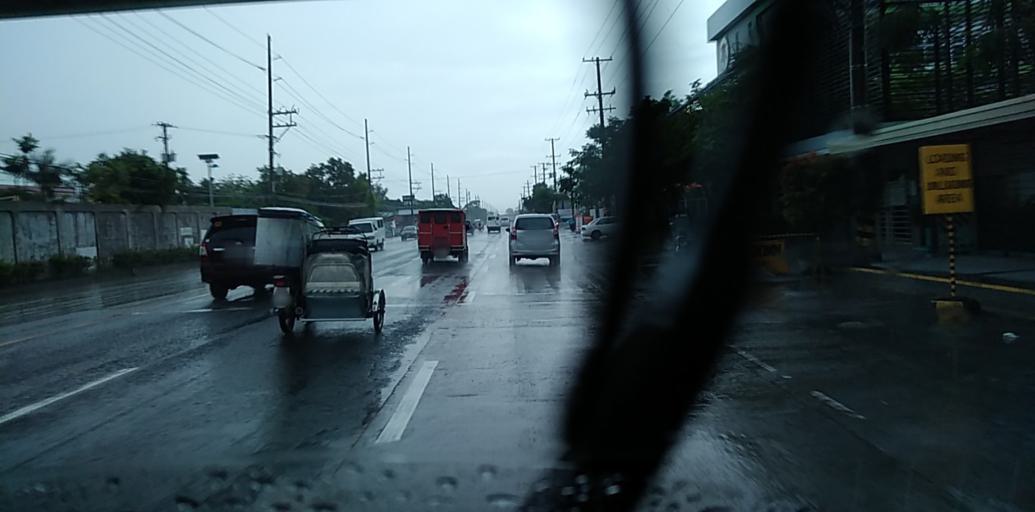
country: PH
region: Central Luzon
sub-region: Province of Pampanga
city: Bulaon
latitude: 15.0623
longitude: 120.6541
